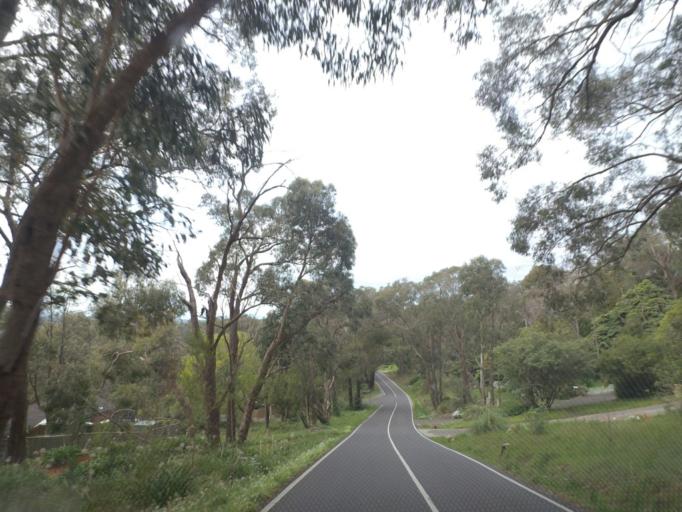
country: AU
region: Victoria
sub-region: Yarra Ranges
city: Montrose
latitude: -37.8183
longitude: 145.3468
